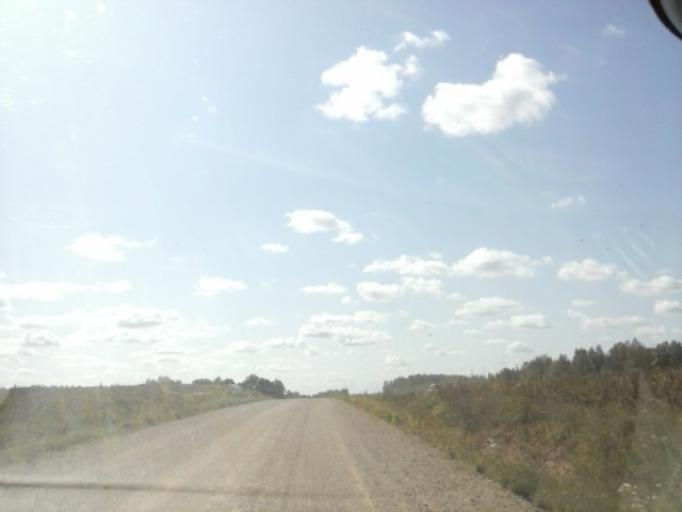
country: EE
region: Polvamaa
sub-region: Polva linn
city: Polva
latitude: 58.1089
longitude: 26.8645
